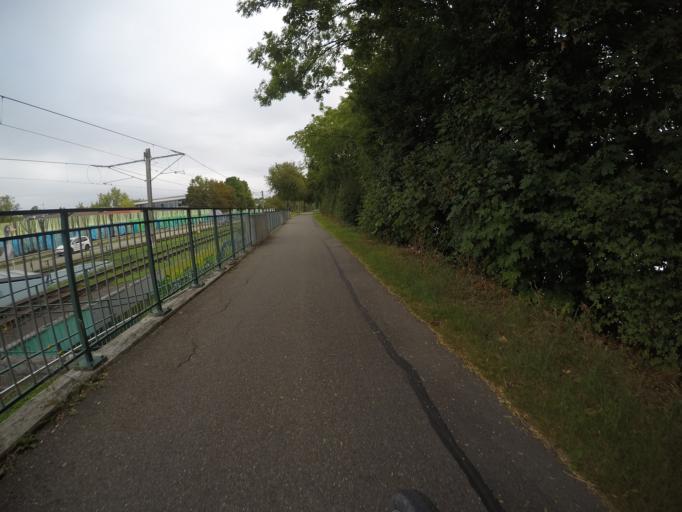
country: DE
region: Baden-Wuerttemberg
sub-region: Regierungsbezirk Stuttgart
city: Stuttgart Muehlhausen
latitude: 48.8618
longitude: 9.2540
